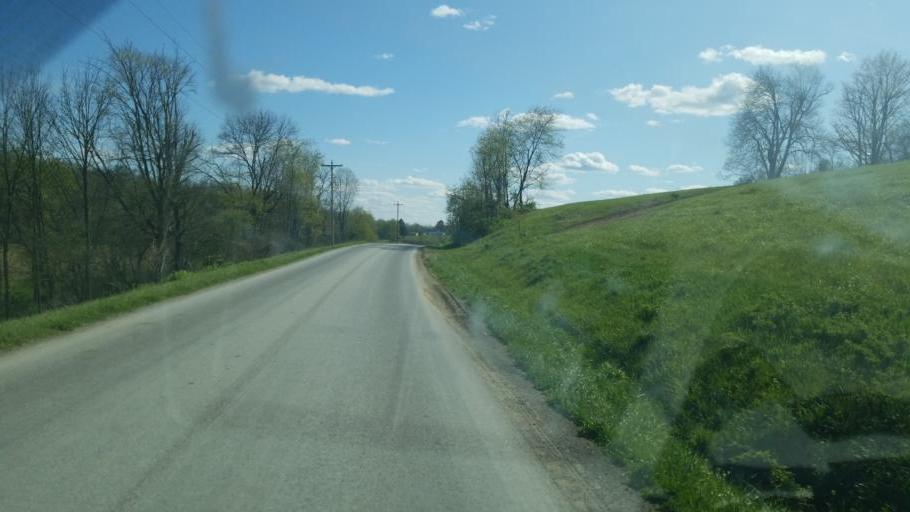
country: US
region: Ohio
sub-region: Coshocton County
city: Coshocton
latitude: 40.4044
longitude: -81.8364
